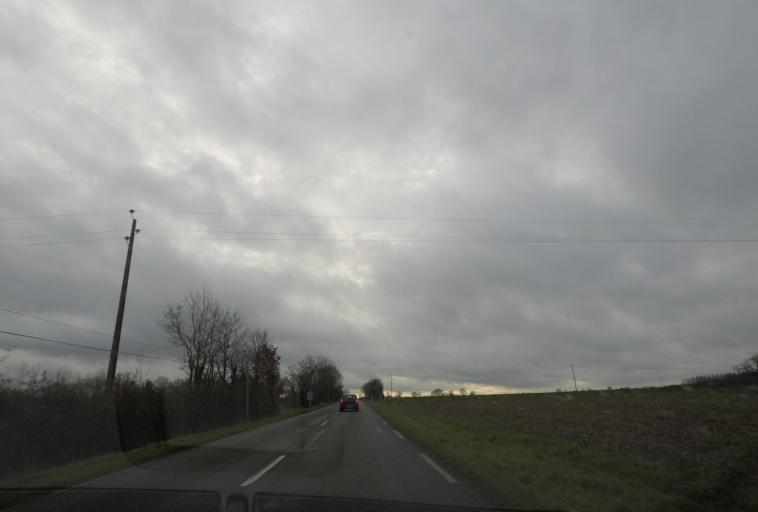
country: FR
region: Pays de la Loire
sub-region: Departement de la Sarthe
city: Vibraye
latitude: 48.0120
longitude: 0.7564
